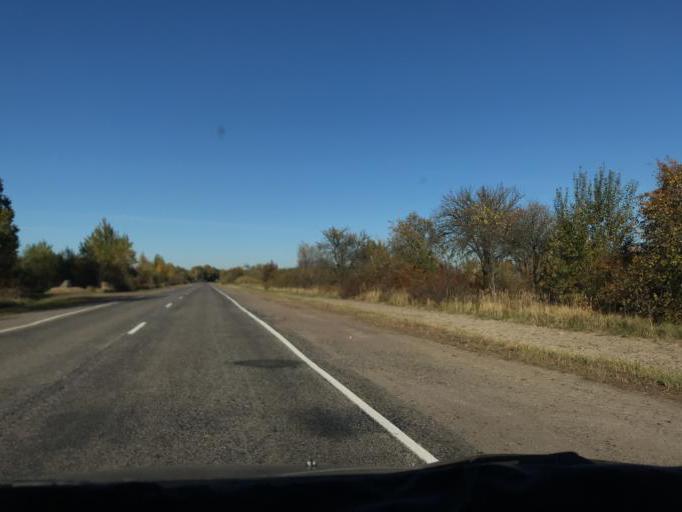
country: BY
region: Gomel
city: Yel'sk
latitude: 51.7320
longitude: 29.1732
